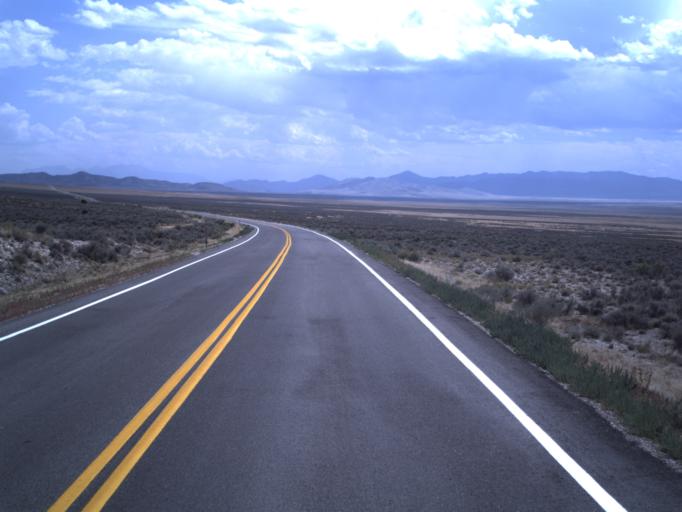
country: US
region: Utah
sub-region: Tooele County
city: Tooele
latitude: 40.2930
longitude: -112.2725
